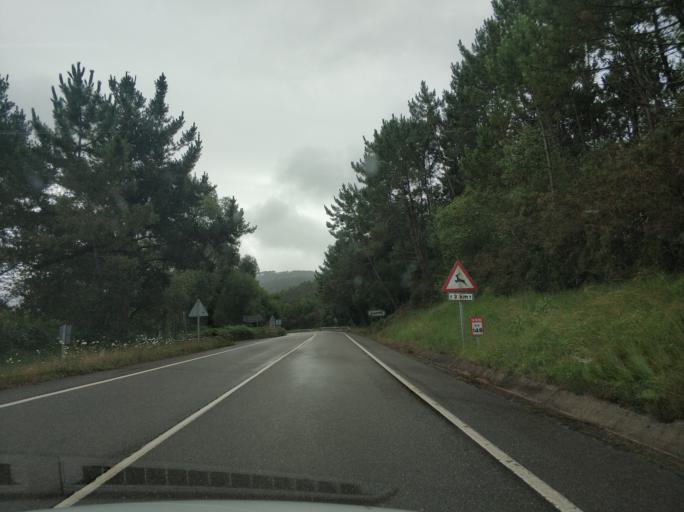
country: ES
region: Asturias
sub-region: Province of Asturias
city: Tineo
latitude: 43.5452
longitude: -6.4336
